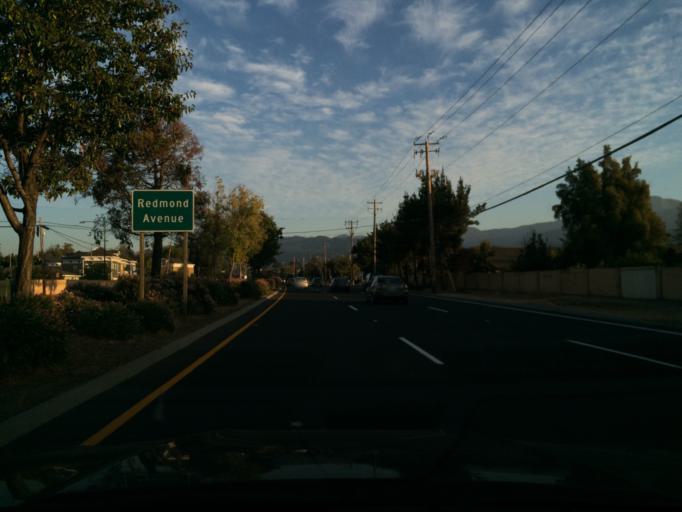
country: US
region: California
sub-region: Santa Clara County
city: Seven Trees
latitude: 37.2318
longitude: -121.8714
